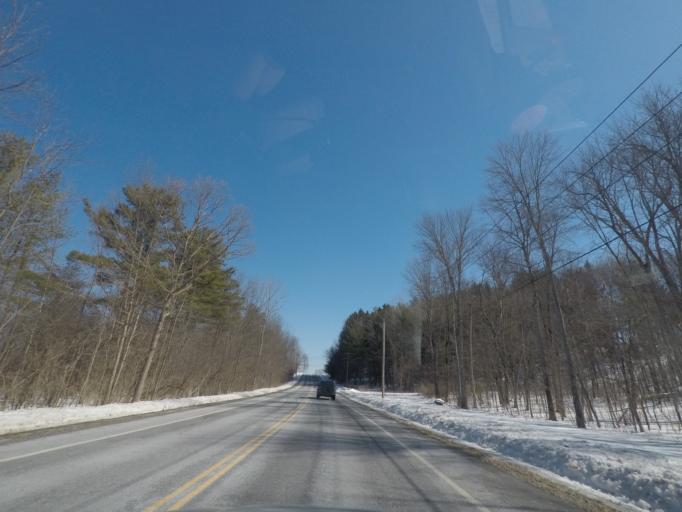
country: US
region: New York
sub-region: Saratoga County
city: Saratoga Springs
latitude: 43.0539
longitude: -73.7604
